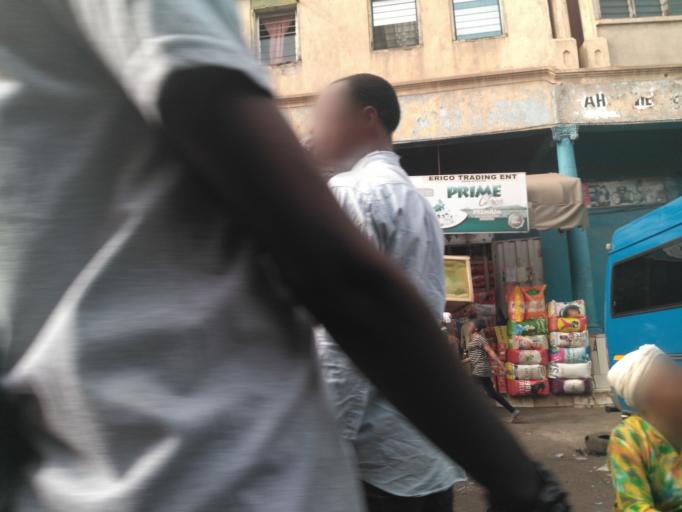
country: GH
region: Ashanti
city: Kumasi
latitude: 6.6971
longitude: -1.6237
